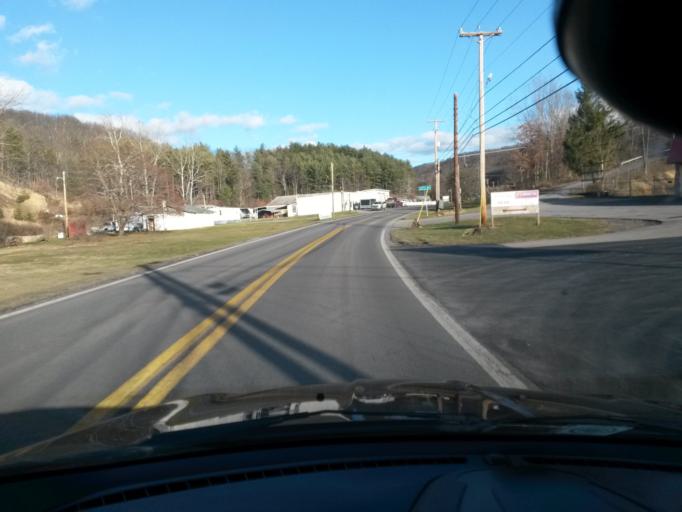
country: US
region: Virginia
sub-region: Giles County
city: Narrows
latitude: 37.4009
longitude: -80.7720
